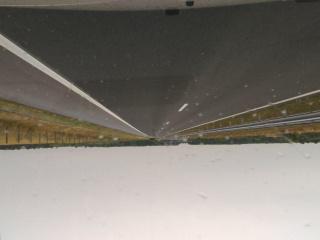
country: BG
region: Stara Zagora
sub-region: Obshtina Stara Zagora
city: Stara Zagora
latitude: 42.3490
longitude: 25.7275
